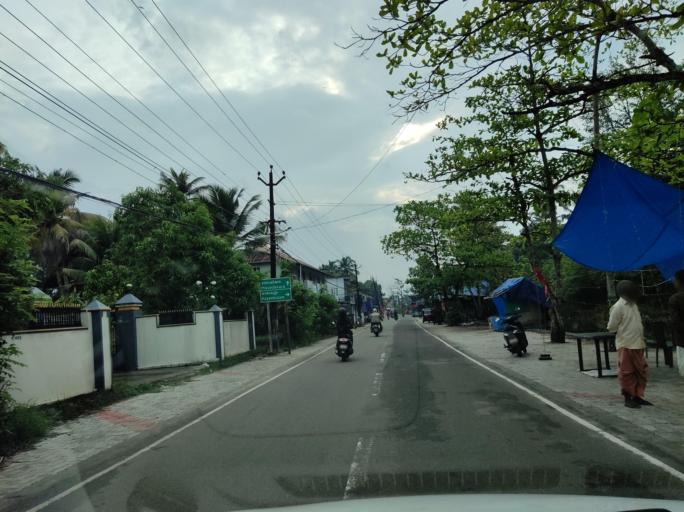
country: IN
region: Kerala
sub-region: Alappuzha
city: Kayankulam
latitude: 9.2598
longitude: 76.4449
